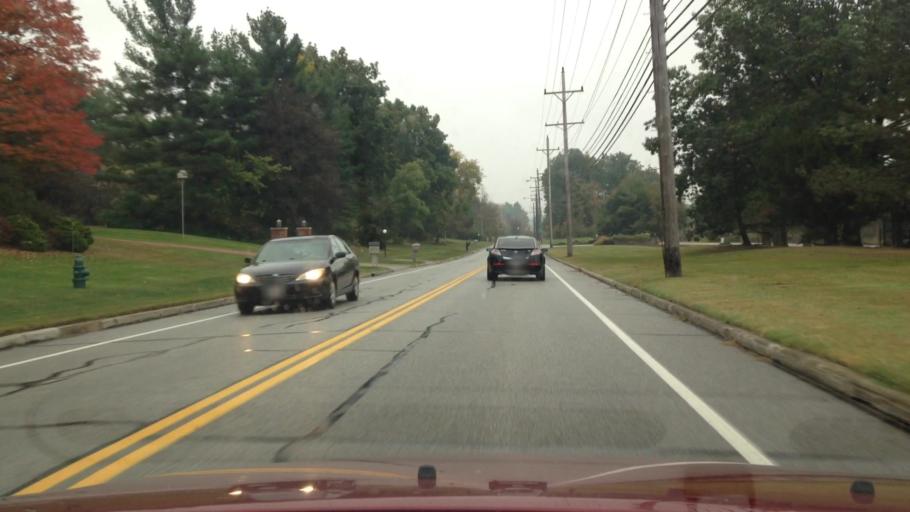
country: US
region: Ohio
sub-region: Cuyahoga County
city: Pepper Pike
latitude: 41.4959
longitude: -81.4630
